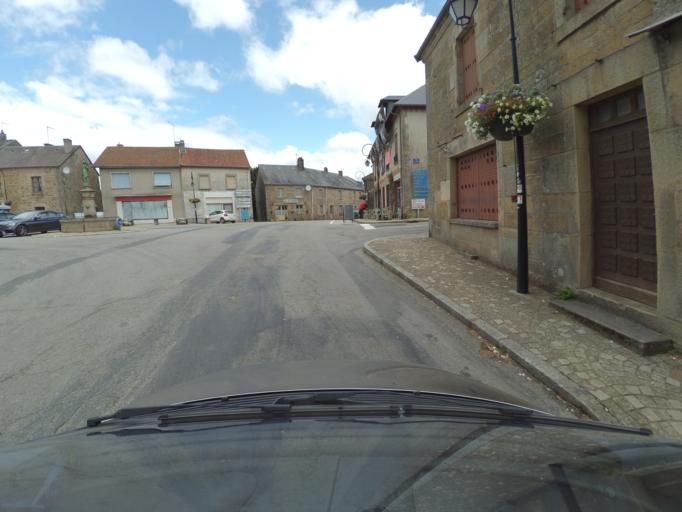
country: FR
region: Limousin
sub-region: Departement de la Haute-Vienne
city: Peyrat-le-Chateau
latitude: 45.8411
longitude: 1.9113
